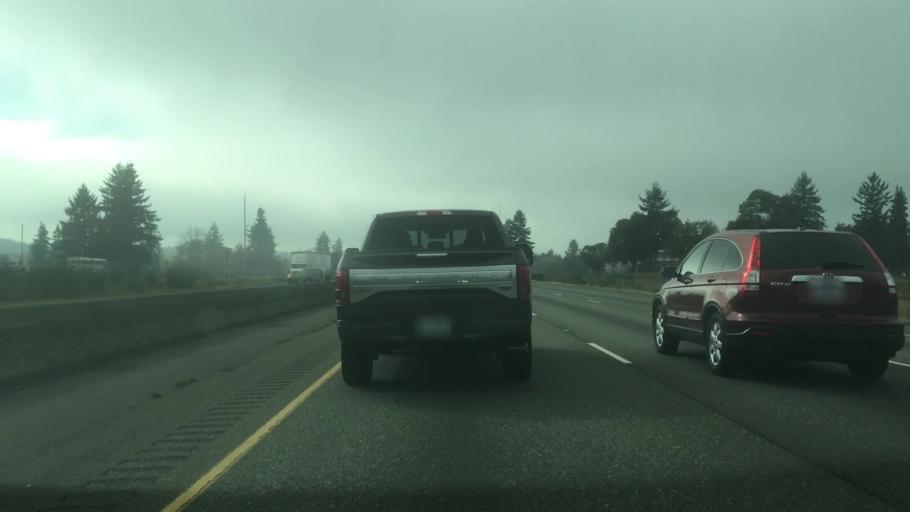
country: US
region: Washington
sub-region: Pierce County
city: DuPont
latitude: 47.0987
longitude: -122.6104
